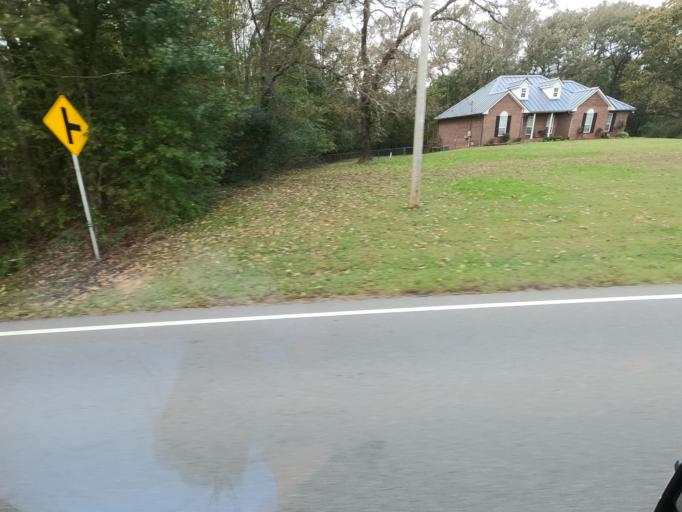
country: US
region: Tennessee
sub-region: Cheatham County
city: Kingston Springs
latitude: 36.1019
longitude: -87.0849
